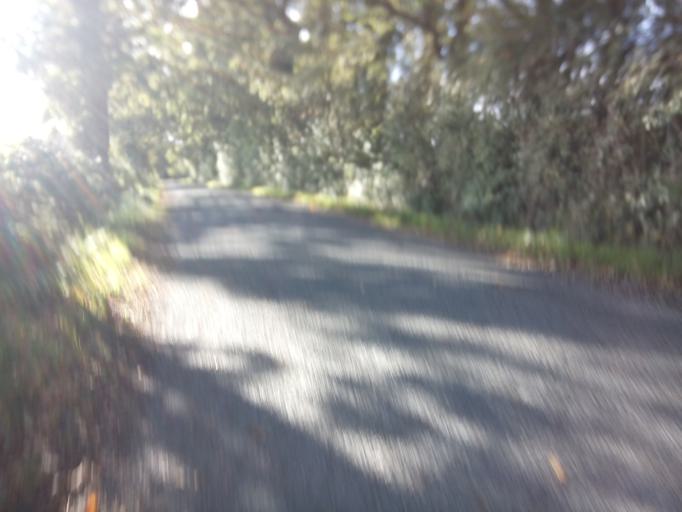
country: GB
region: England
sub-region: Suffolk
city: Lavenham
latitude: 52.0565
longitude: 0.8653
